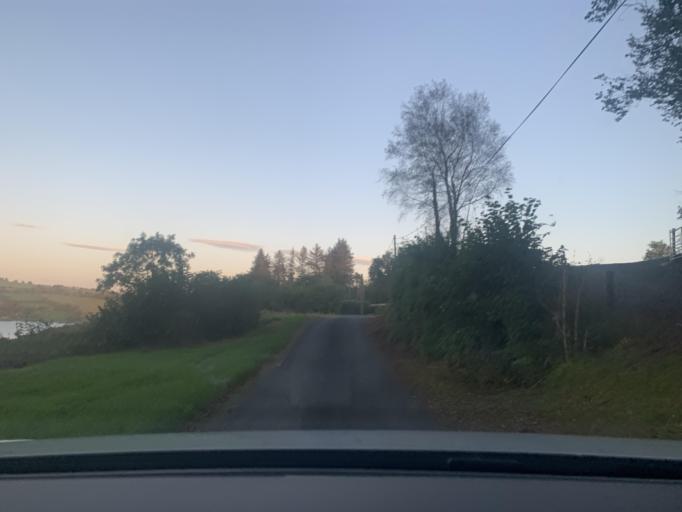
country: IE
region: Connaught
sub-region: Sligo
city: Sligo
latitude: 54.2727
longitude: -8.4082
